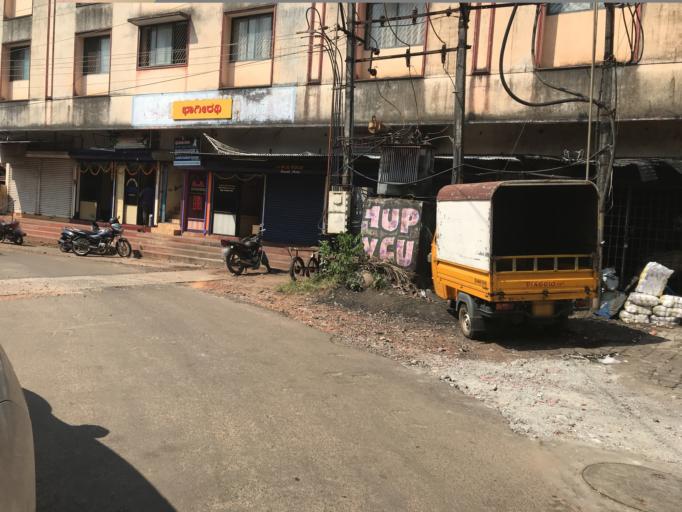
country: IN
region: Karnataka
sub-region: Dakshina Kannada
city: Mangalore
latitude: 12.8679
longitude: 74.8375
